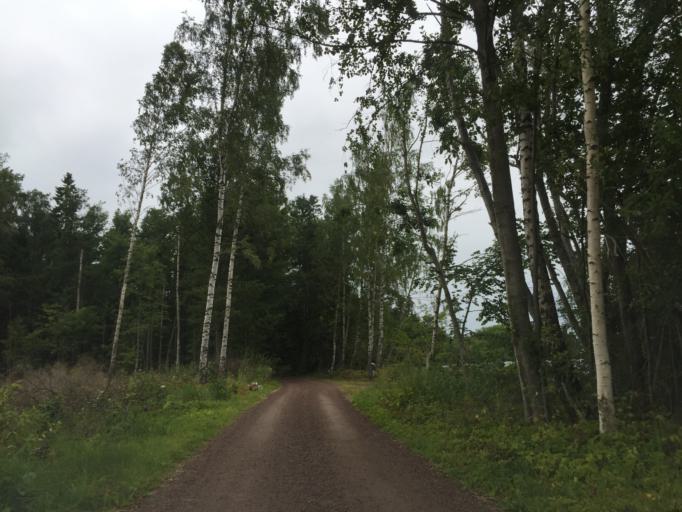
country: SE
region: OEstergoetland
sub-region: Vadstena Kommun
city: Vadstena
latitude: 58.4738
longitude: 14.8319
